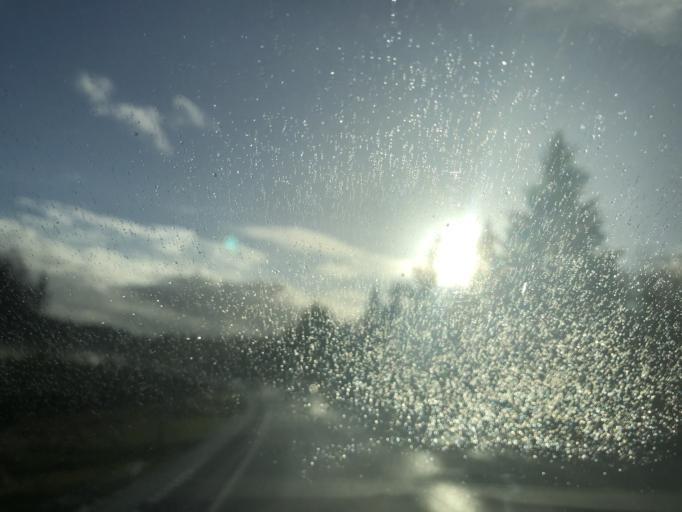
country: US
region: Washington
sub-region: Kitsap County
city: Silverdale
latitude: 47.6580
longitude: -122.7043
